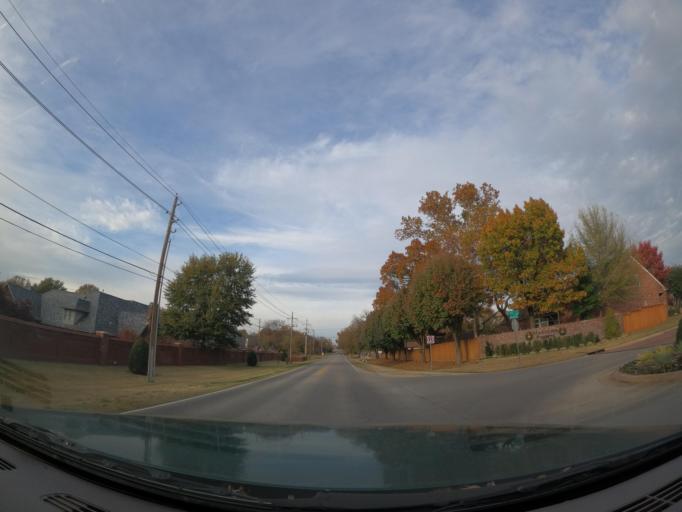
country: US
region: Oklahoma
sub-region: Tulsa County
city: Jenks
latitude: 36.0383
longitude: -95.9400
